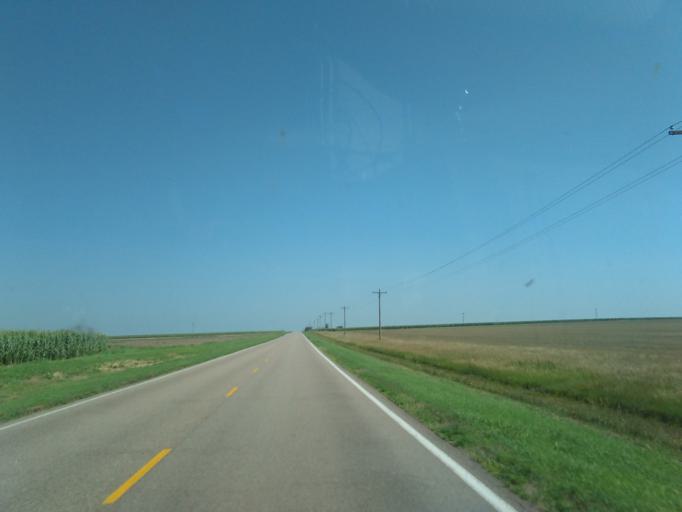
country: US
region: Kansas
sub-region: Cheyenne County
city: Saint Francis
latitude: 39.7824
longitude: -101.5420
